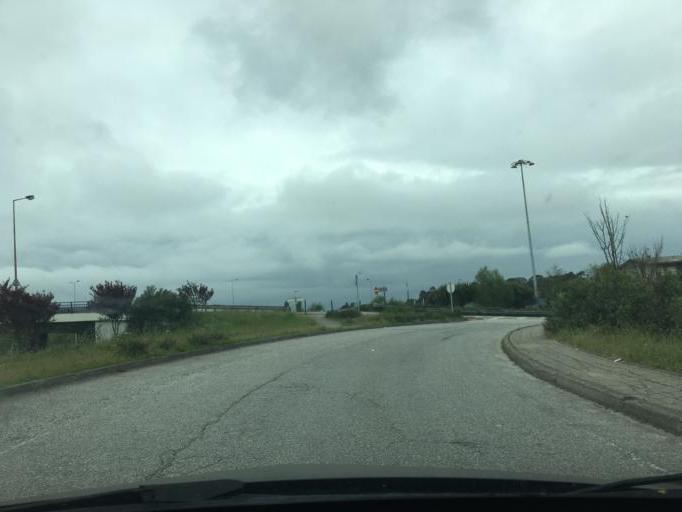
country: PT
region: Porto
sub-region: Matosinhos
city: Santa Cruz do Bispo
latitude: 41.2174
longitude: -8.6891
